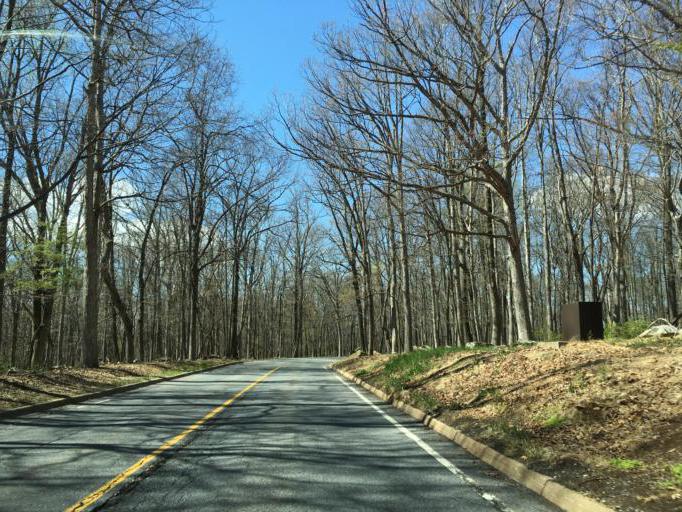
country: US
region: Maryland
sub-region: Frederick County
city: Thurmont
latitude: 39.6439
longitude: -77.4715
